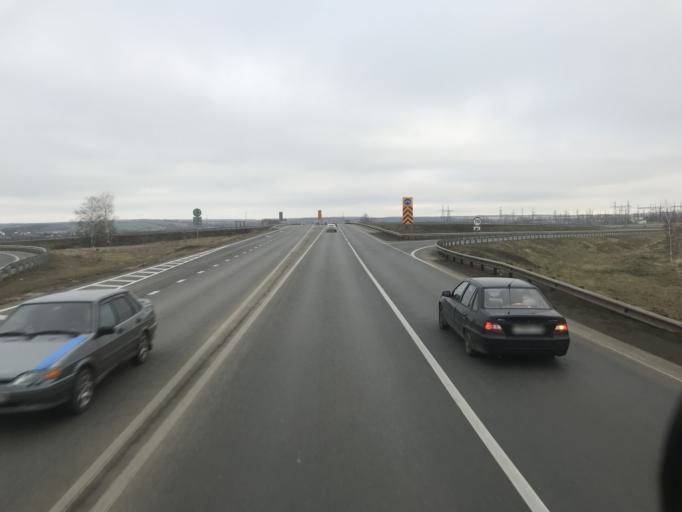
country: RU
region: Penza
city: Bogoslovka
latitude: 53.1307
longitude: 44.7745
